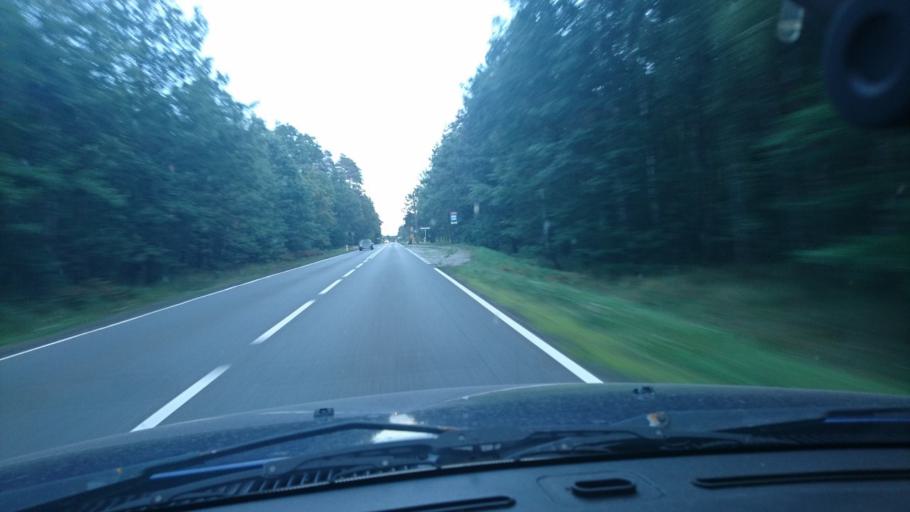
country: PL
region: Silesian Voivodeship
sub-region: Powiat tarnogorski
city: Tworog
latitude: 50.5096
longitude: 18.7525
